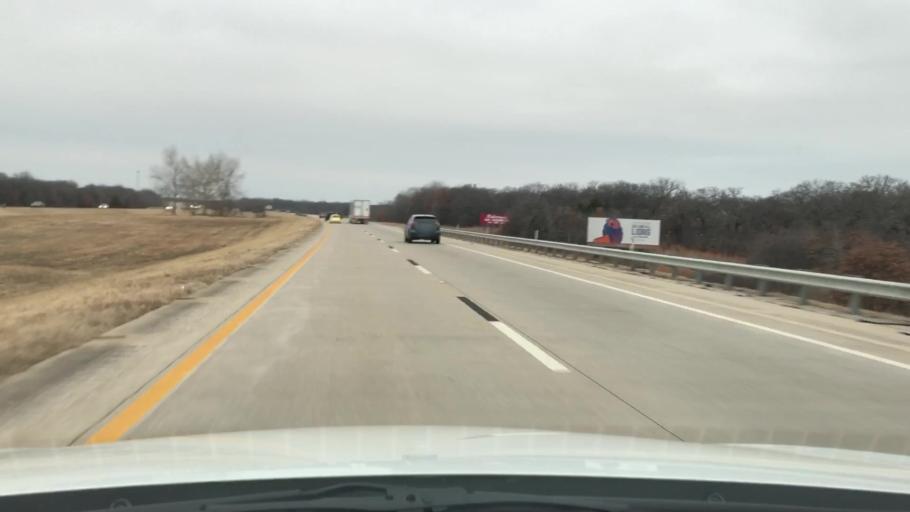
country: US
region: Oklahoma
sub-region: Love County
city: Marietta
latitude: 33.8212
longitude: -97.1302
